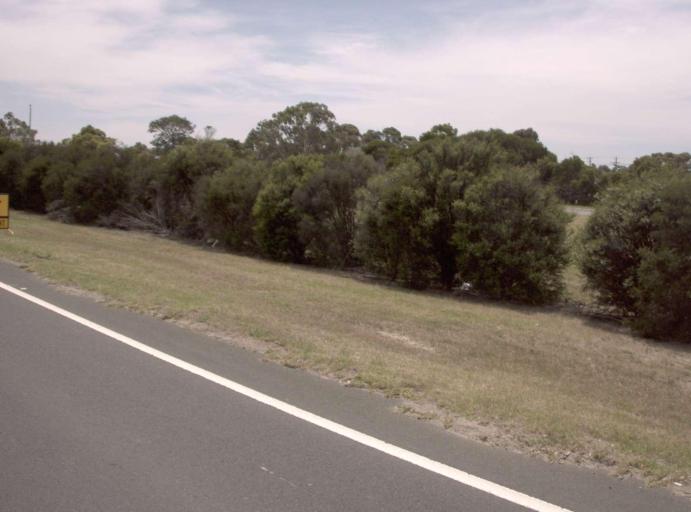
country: AU
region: Victoria
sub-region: Casey
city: Hampton Park
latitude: -38.0384
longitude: 145.2467
